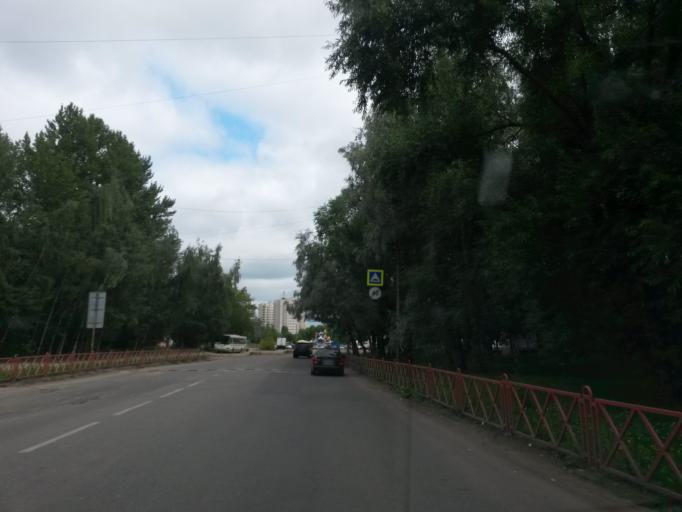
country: RU
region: Jaroslavl
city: Yaroslavl
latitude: 57.5736
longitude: 39.8621
